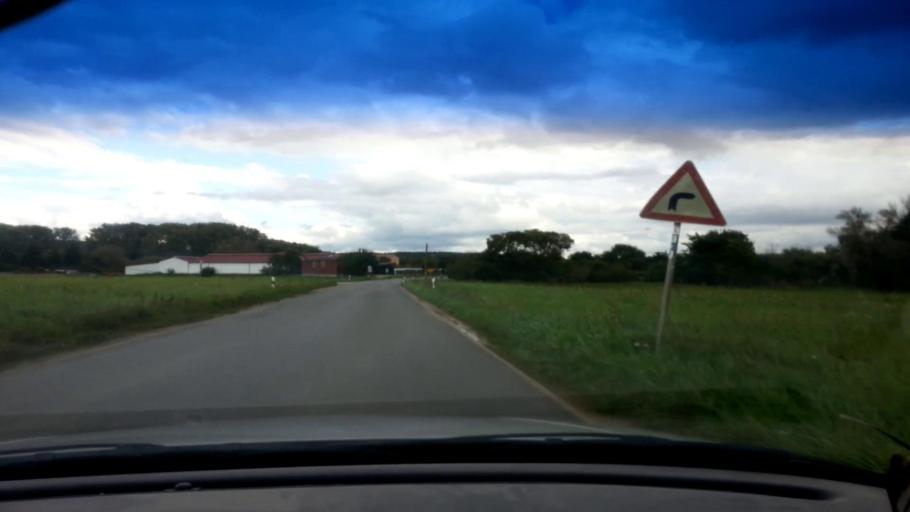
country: DE
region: Bavaria
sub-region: Upper Franconia
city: Zapfendorf
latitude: 50.0227
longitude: 10.9260
